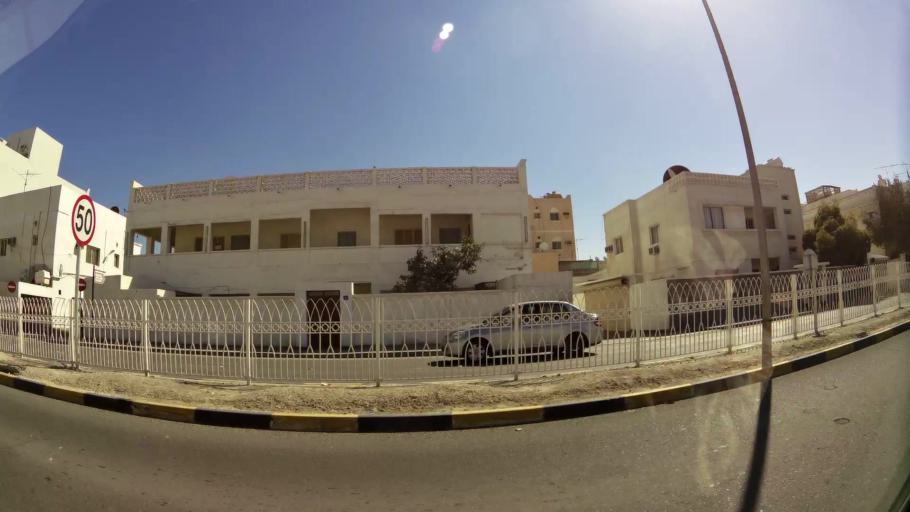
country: BH
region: Muharraq
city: Al Muharraq
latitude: 26.2559
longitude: 50.6080
